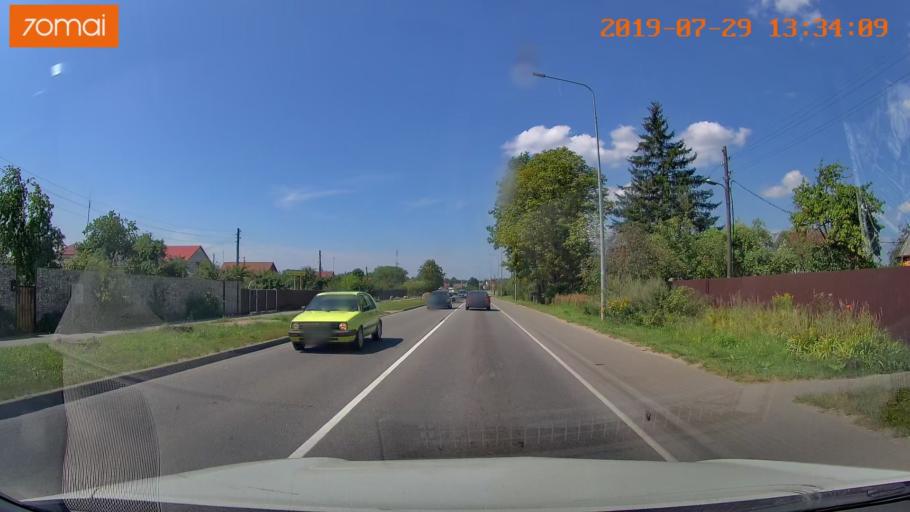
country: RU
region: Kaliningrad
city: Volochayevskoye
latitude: 54.7001
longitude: 20.2198
